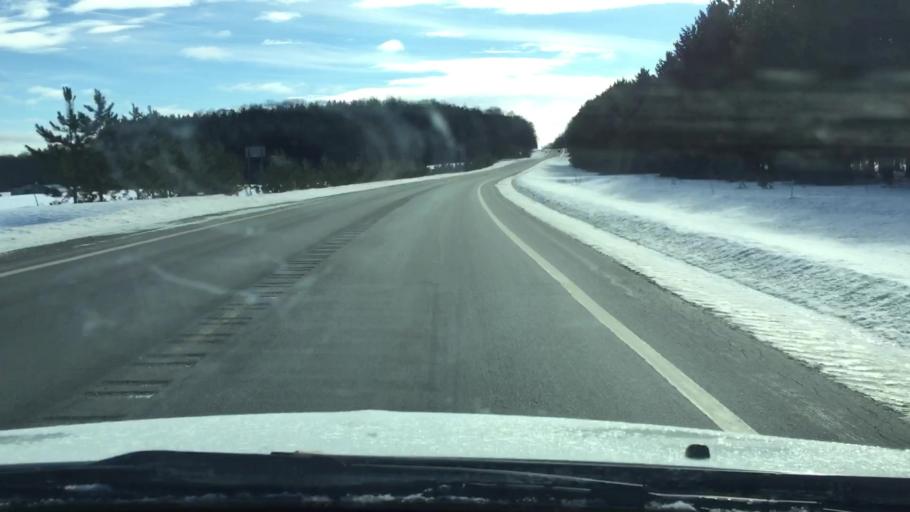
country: US
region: Michigan
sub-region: Antrim County
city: Mancelona
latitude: 44.9809
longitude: -85.0537
